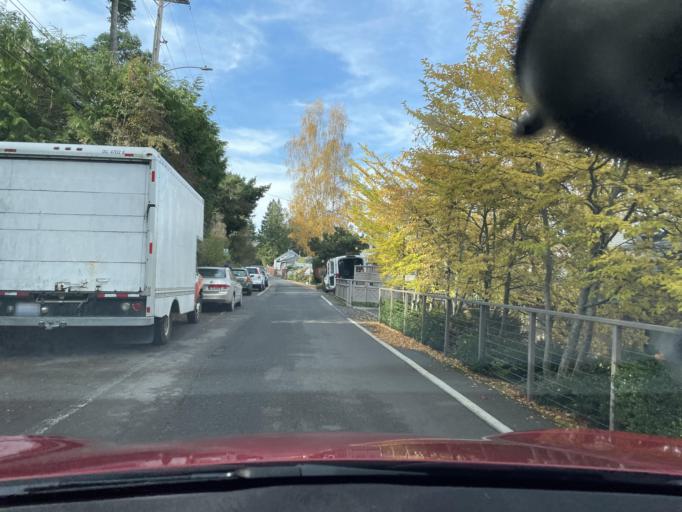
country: US
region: Washington
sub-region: San Juan County
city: Friday Harbor
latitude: 48.5335
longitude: -123.0081
